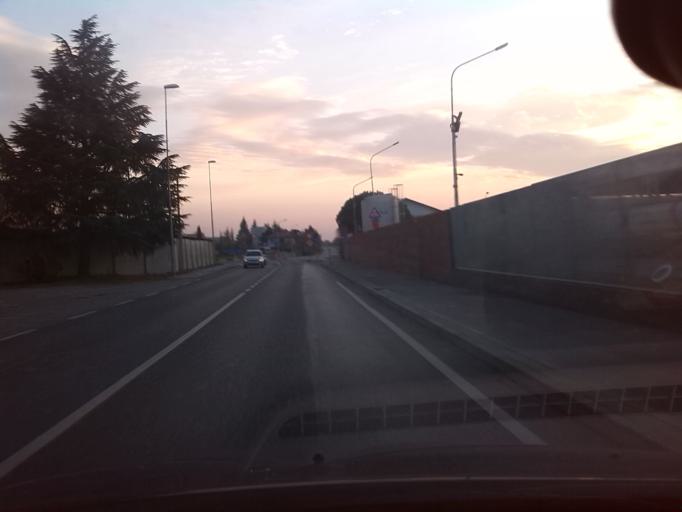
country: IT
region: Friuli Venezia Giulia
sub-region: Provincia di Udine
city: Basaldella
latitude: 46.0266
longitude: 13.2151
